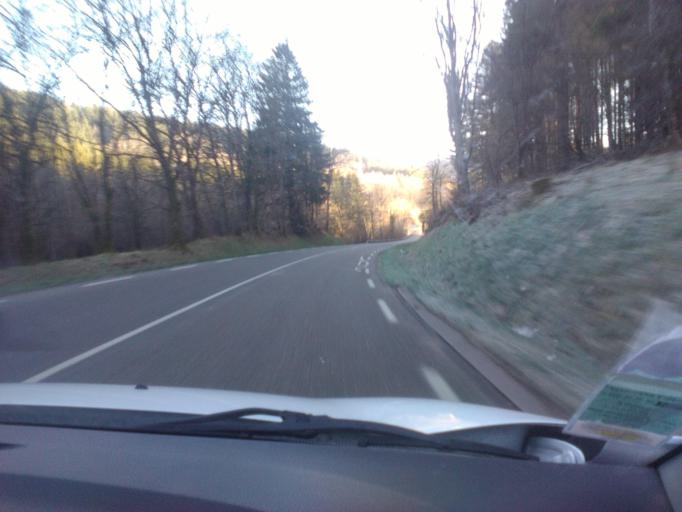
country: FR
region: Alsace
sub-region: Departement du Bas-Rhin
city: Rothau
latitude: 48.4166
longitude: 7.1743
